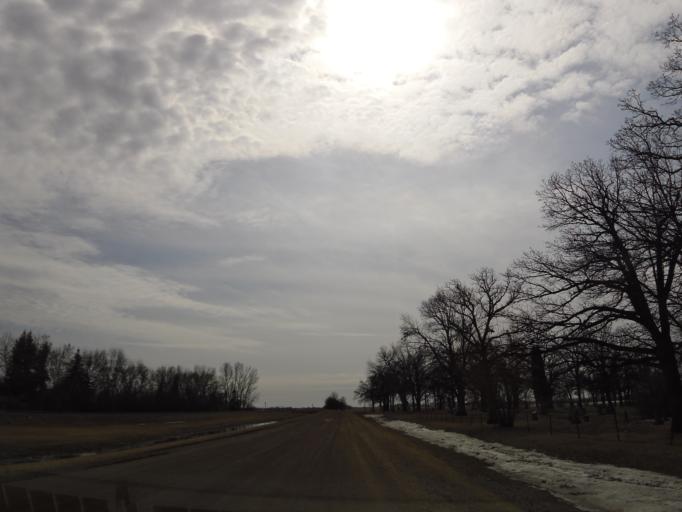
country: US
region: North Dakota
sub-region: Walsh County
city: Grafton
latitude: 48.2833
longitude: -97.3670
